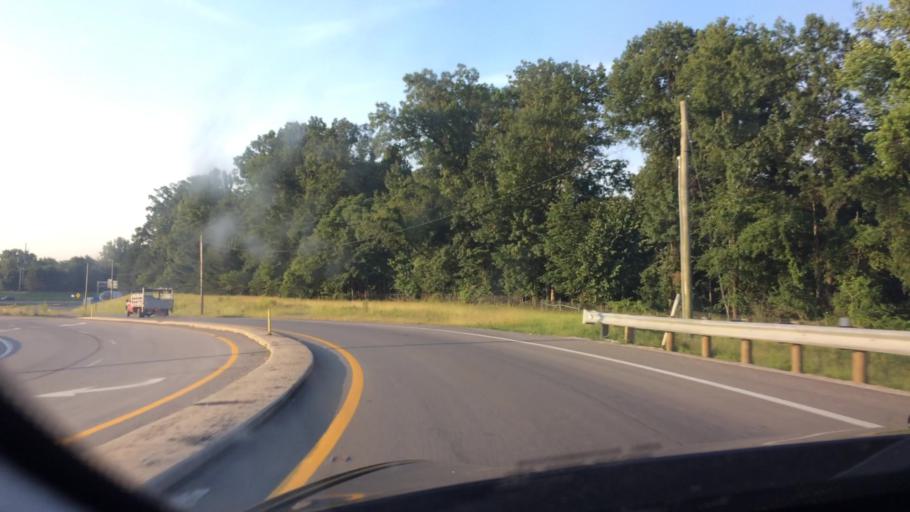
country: US
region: Ohio
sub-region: Lucas County
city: Holland
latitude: 41.6118
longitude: -83.6937
